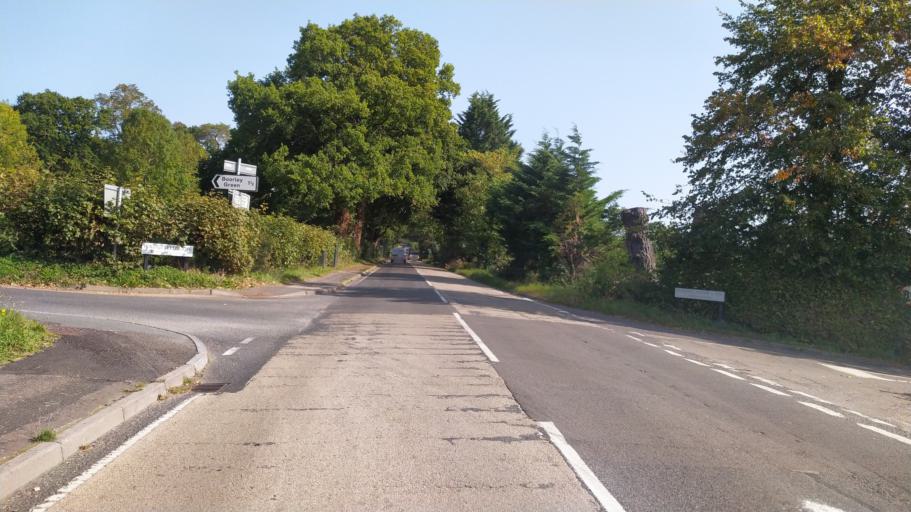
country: GB
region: England
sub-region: Hampshire
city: Botley
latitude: 50.9207
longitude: -1.2515
